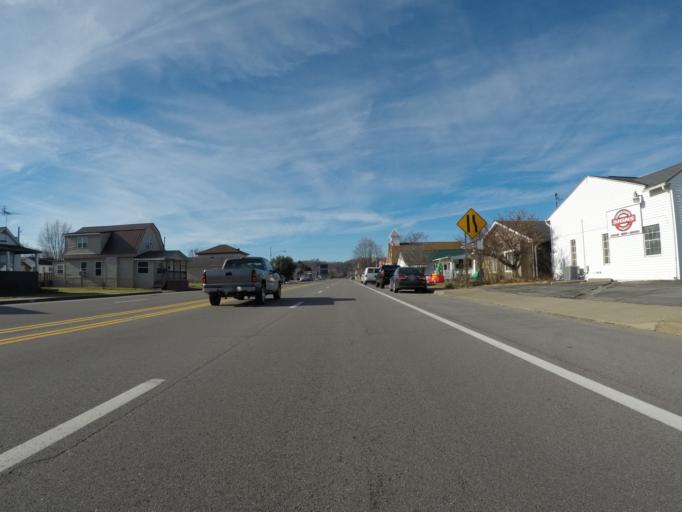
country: US
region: West Virginia
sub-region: Wayne County
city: Kenova
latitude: 38.4024
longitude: -82.5816
